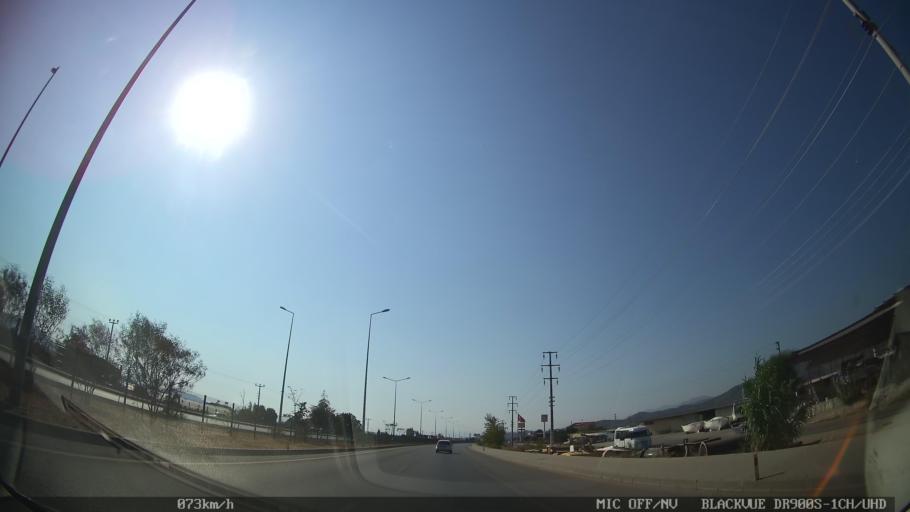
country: TR
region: Mugla
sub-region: Fethiye
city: Fethiye
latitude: 36.6555
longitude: 29.1636
